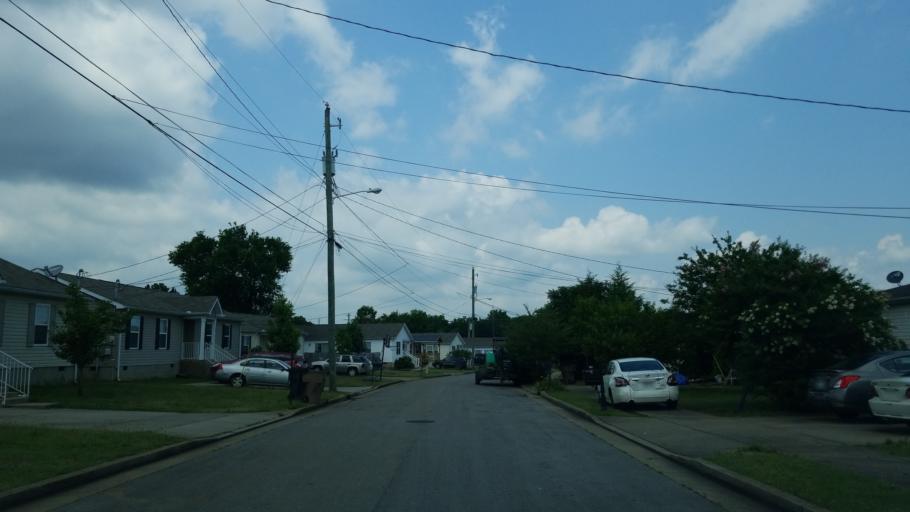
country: US
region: Tennessee
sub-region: Rutherford County
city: La Vergne
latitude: 36.0535
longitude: -86.5838
